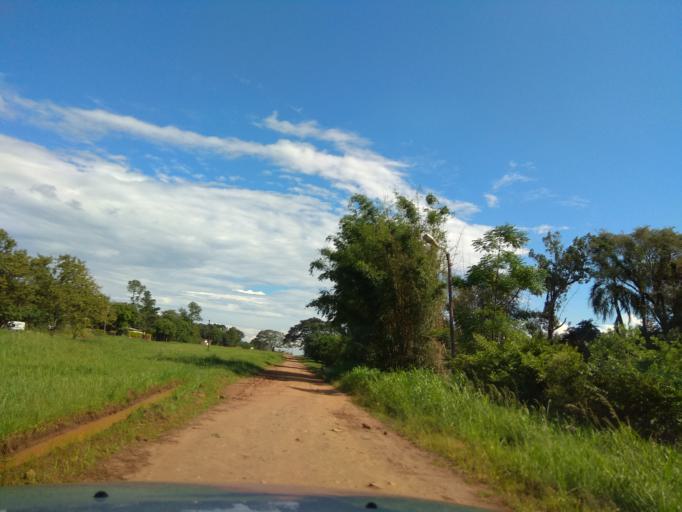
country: AR
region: Misiones
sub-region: Departamento de Candelaria
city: Candelaria
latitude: -27.4575
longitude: -55.7550
